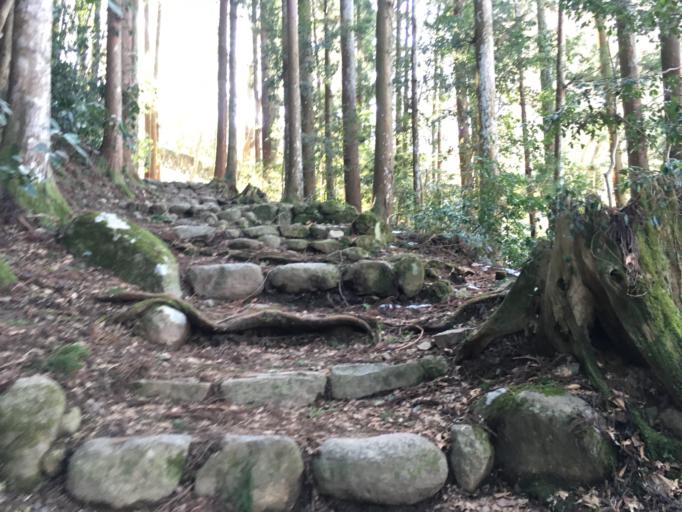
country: JP
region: Shimane
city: Masuda
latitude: 34.4609
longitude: 131.7642
